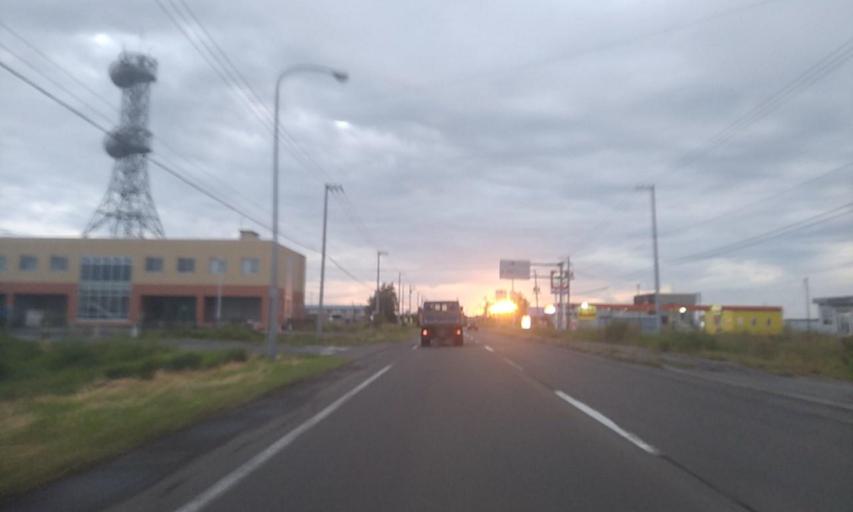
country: JP
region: Hokkaido
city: Abashiri
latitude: 43.9003
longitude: 144.6520
